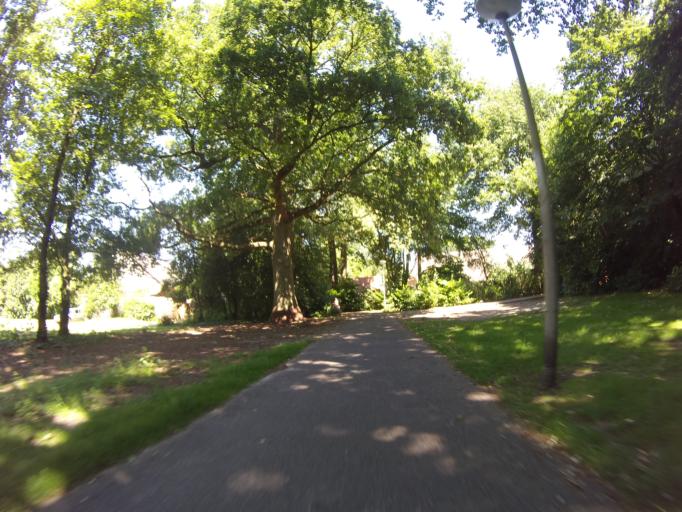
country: NL
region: Drenthe
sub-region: Gemeente Emmen
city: Emmen
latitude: 52.7721
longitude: 6.8863
